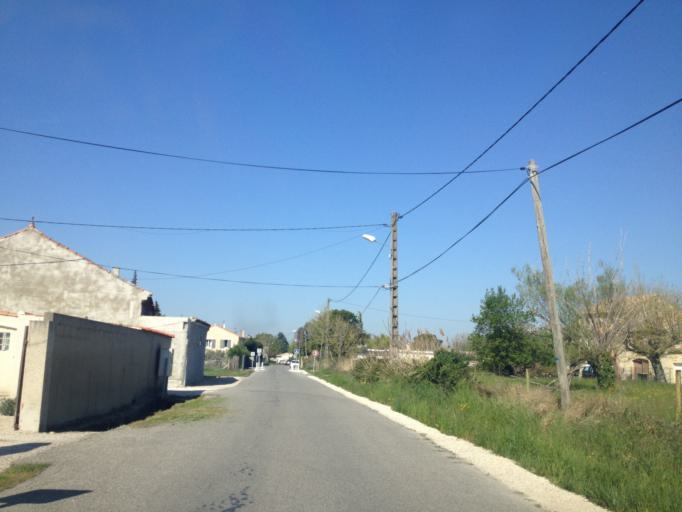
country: FR
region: Provence-Alpes-Cote d'Azur
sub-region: Departement du Vaucluse
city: Jonquieres
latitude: 44.1176
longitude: 4.8943
